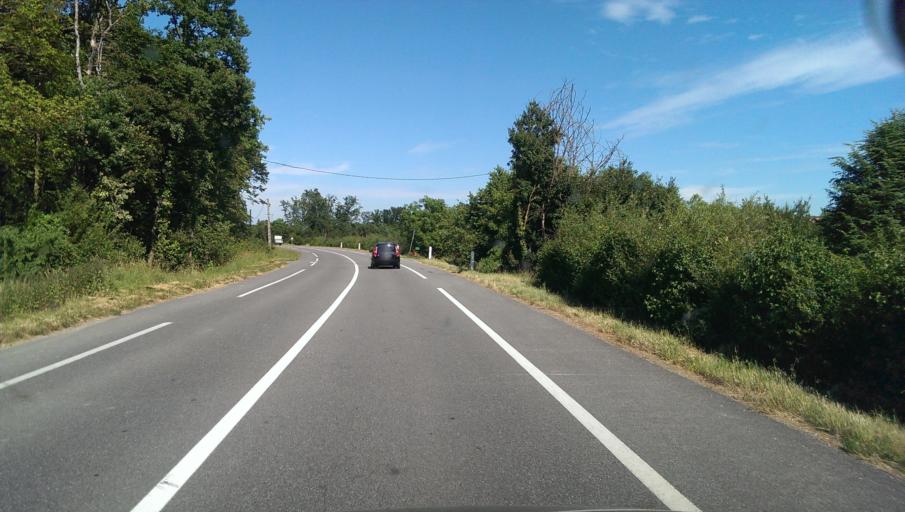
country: FR
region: Alsace
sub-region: Departement du Bas-Rhin
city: Monswiller
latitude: 48.7421
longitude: 7.3992
